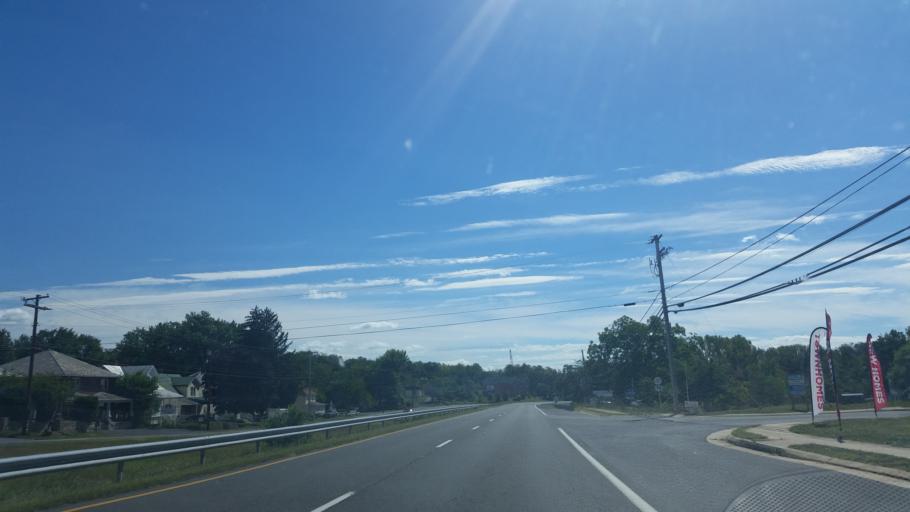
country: US
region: Virginia
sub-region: City of Winchester
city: Winchester
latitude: 39.2068
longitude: -78.1704
